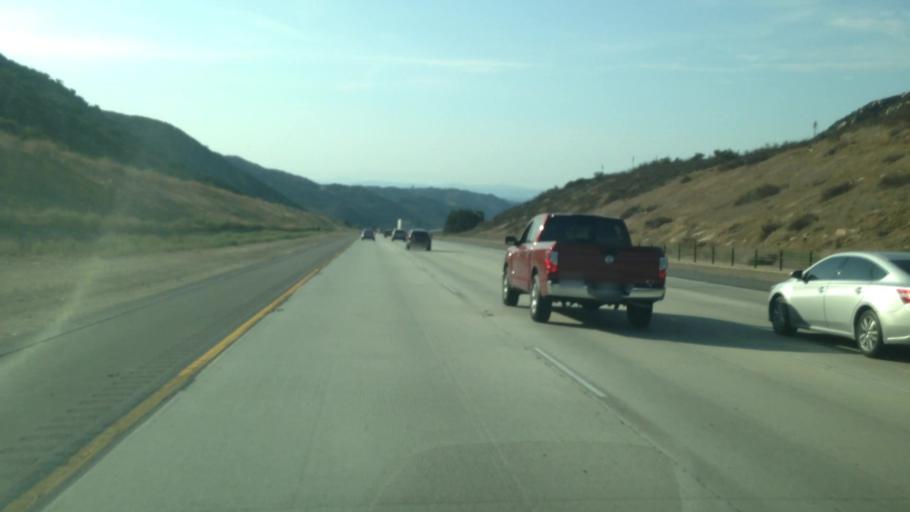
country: US
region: California
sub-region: San Diego County
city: Hidden Meadows
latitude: 33.2092
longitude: -117.1334
